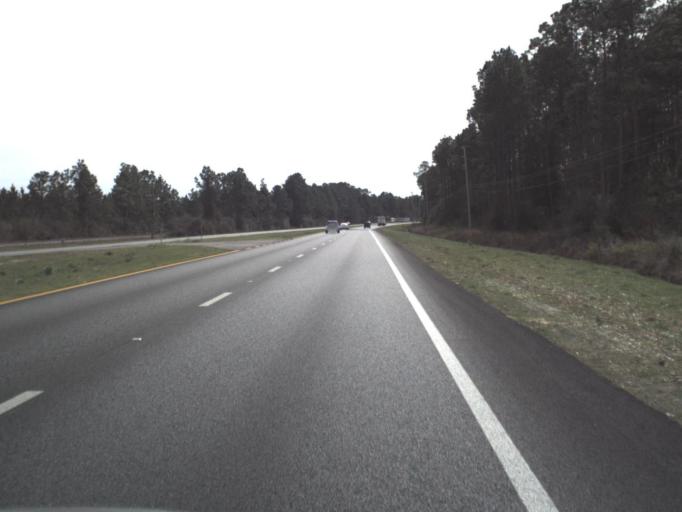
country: US
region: Florida
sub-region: Bay County
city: Youngstown
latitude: 30.4138
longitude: -85.4307
